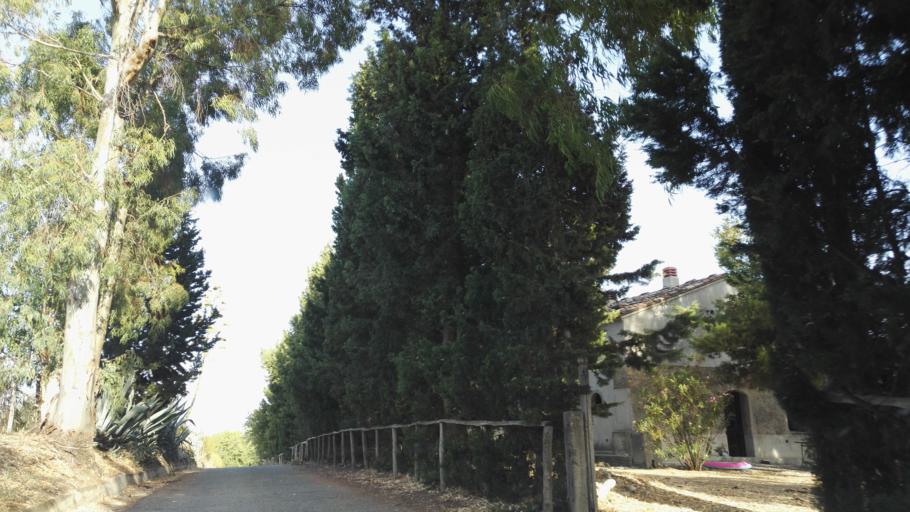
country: IT
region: Calabria
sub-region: Provincia di Reggio Calabria
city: Riace Marina
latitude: 38.3747
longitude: 16.4975
